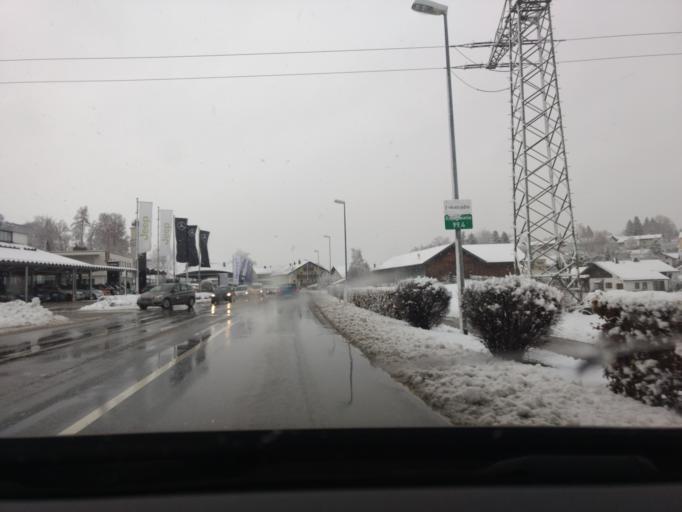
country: DE
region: Bavaria
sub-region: Upper Bavaria
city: Vachendorf
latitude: 47.8578
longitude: 12.6287
